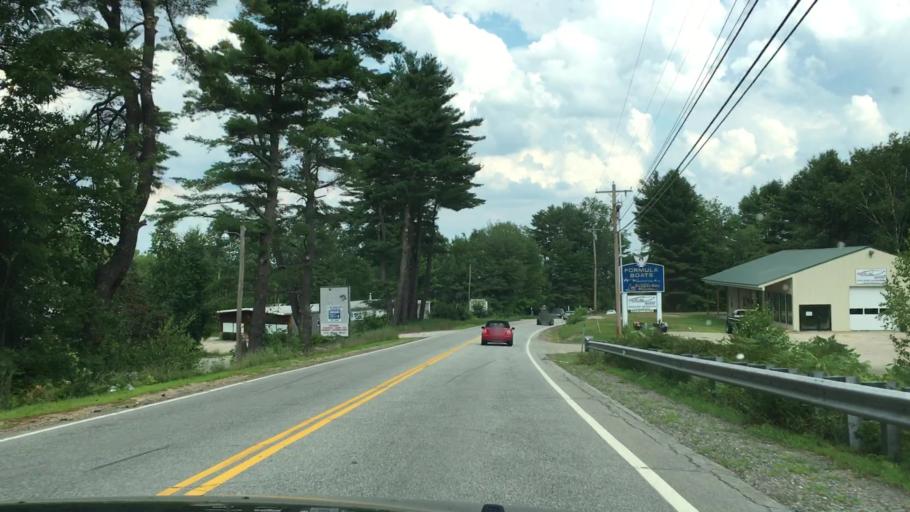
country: US
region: New Hampshire
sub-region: Belknap County
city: Meredith
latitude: 43.6372
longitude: -71.4929
